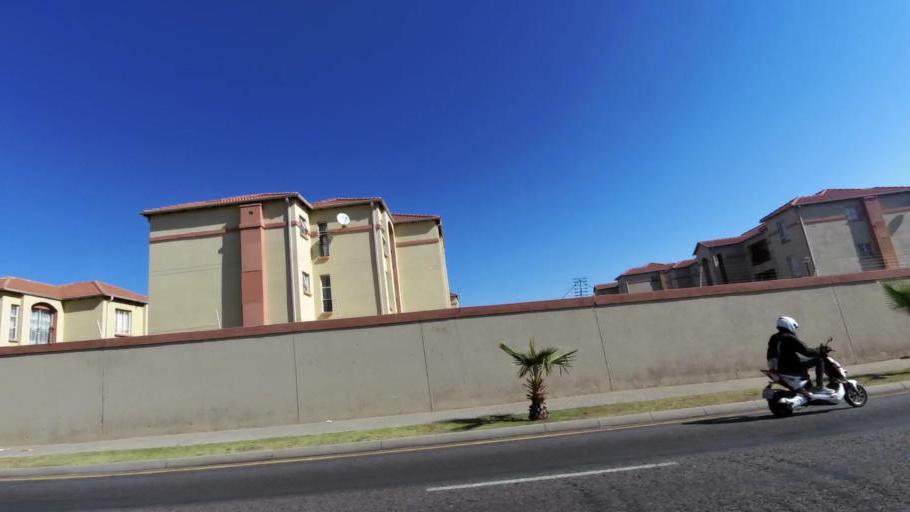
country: ZA
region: Gauteng
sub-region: City of Johannesburg Metropolitan Municipality
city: Johannesburg
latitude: -26.2545
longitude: 27.9854
